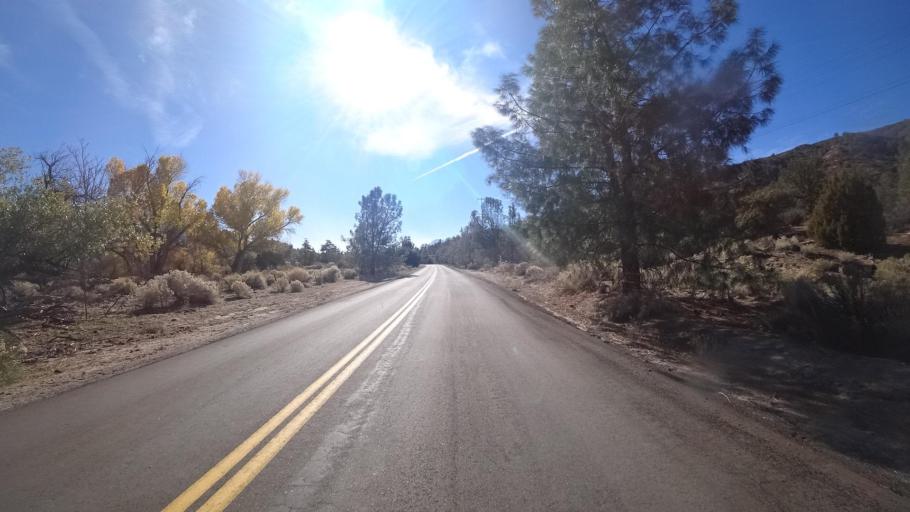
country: US
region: California
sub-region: Kern County
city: Bodfish
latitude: 35.5231
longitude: -118.5110
